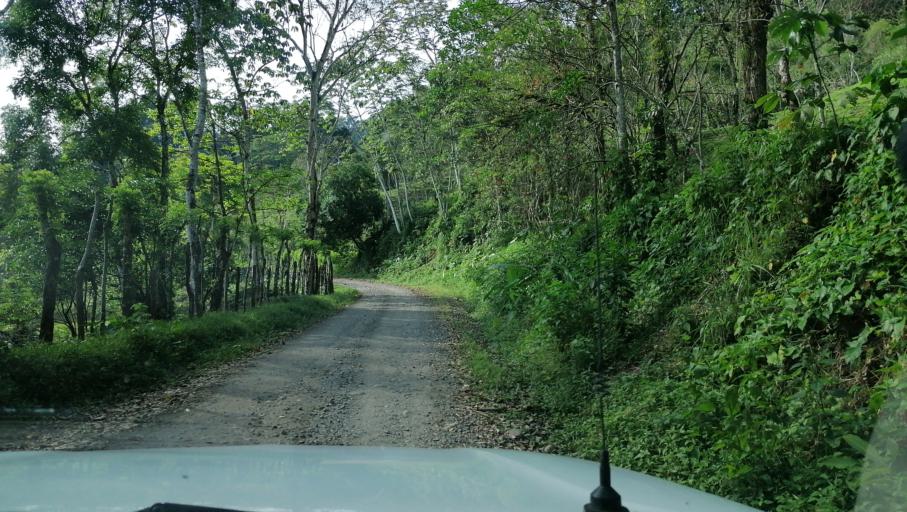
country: MX
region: Chiapas
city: Ostuacan
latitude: 17.4747
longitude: -93.2379
